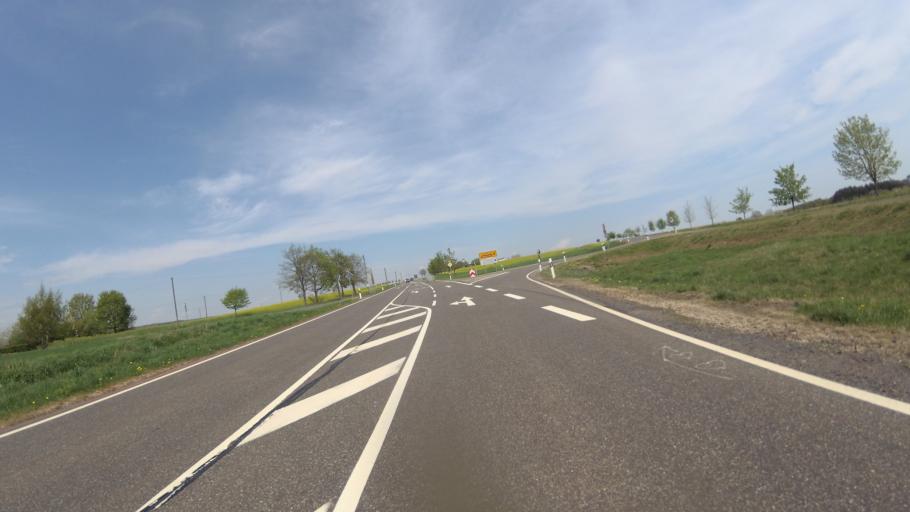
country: DE
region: Rheinland-Pfalz
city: Strotzbusch
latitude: 50.0995
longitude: 6.9650
